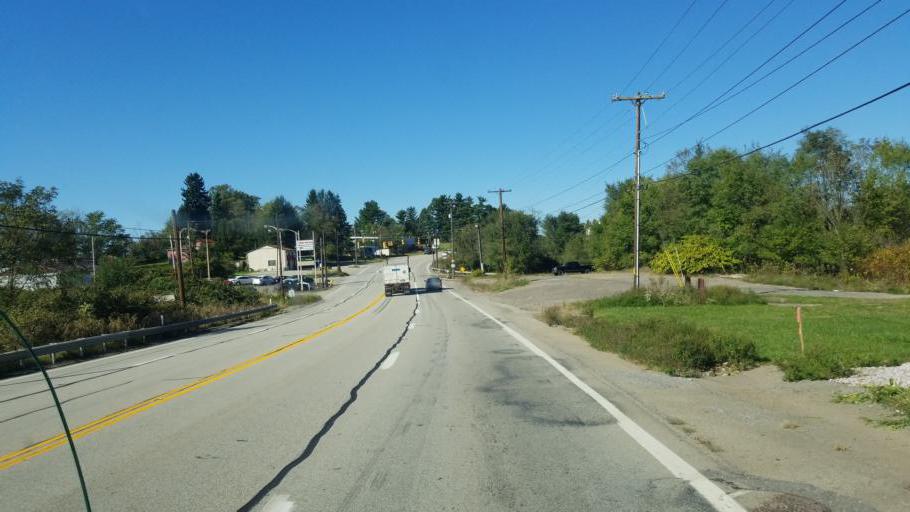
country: US
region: Pennsylvania
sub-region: Westmoreland County
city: Trafford
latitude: 40.3549
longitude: -79.7690
